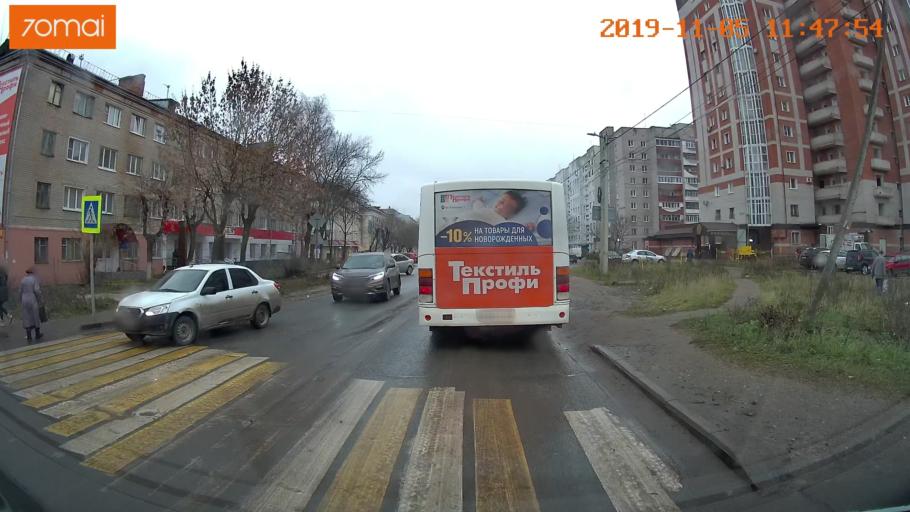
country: RU
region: Ivanovo
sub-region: Gorod Ivanovo
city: Ivanovo
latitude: 57.0095
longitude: 40.9954
